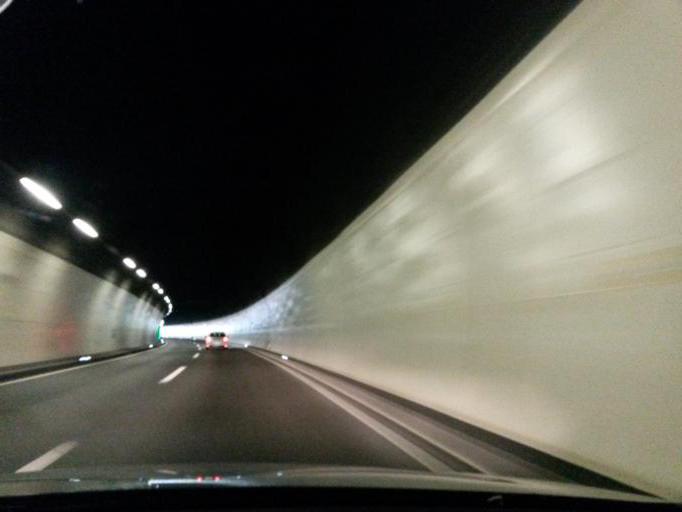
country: CH
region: Ticino
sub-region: Lugano District
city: Melide
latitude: 45.9436
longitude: 8.9657
